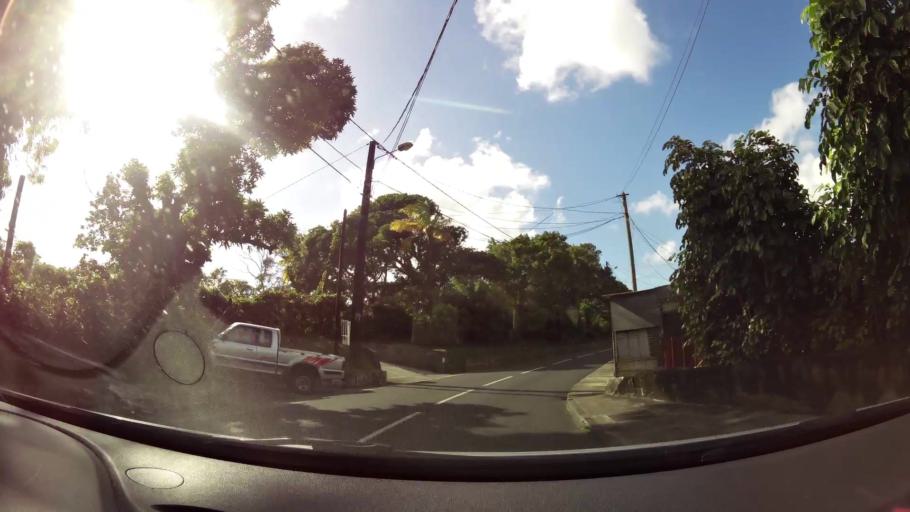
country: MQ
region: Martinique
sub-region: Martinique
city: Fort-de-France
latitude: 14.6425
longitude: -61.0769
